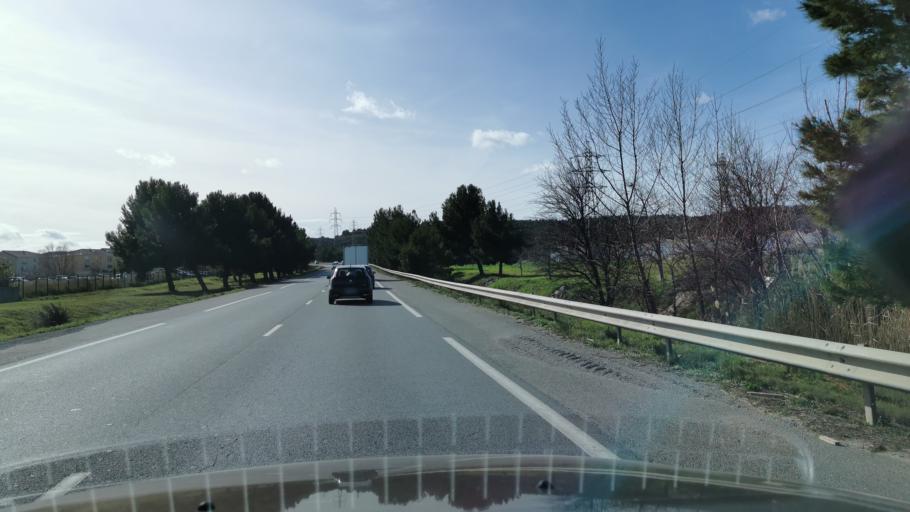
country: FR
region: Languedoc-Roussillon
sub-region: Departement de l'Aude
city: Narbonne
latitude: 43.1914
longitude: 2.9779
